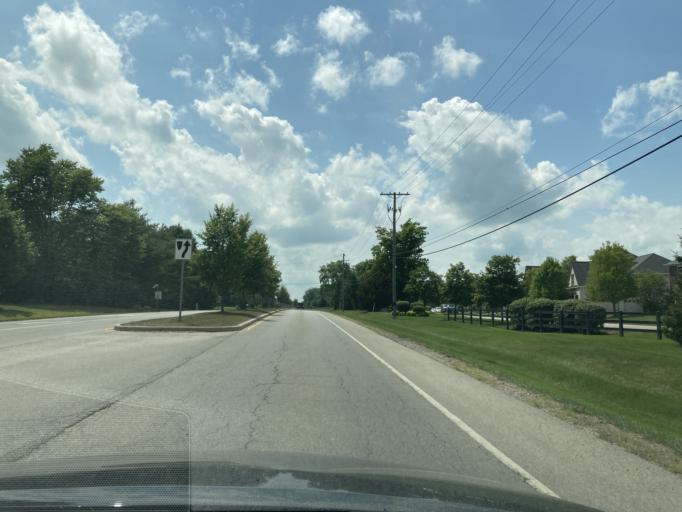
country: US
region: Indiana
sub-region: Boone County
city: Zionsville
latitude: 39.9987
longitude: -86.2520
